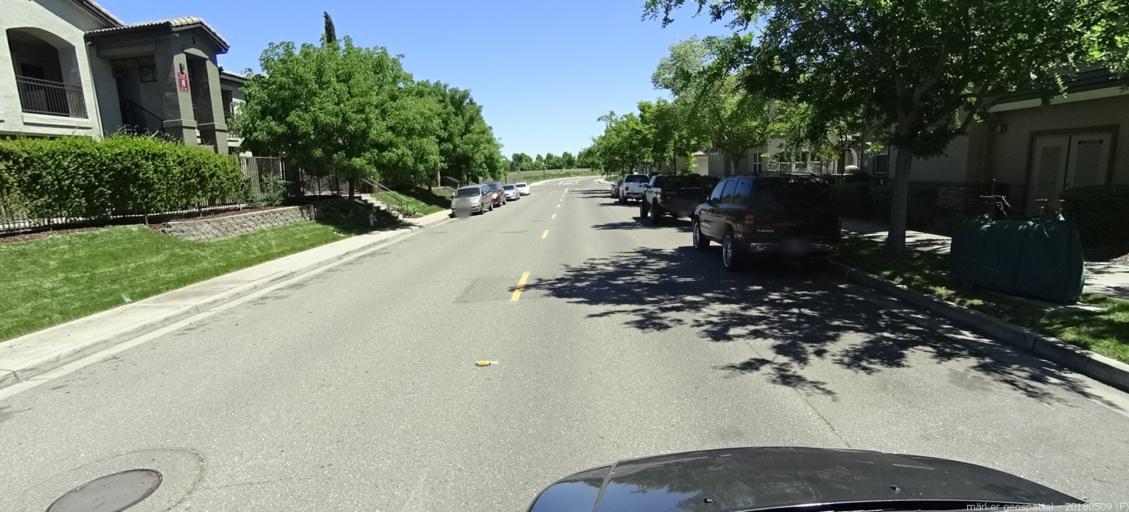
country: US
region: California
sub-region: Sacramento County
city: Sacramento
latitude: 38.6433
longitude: -121.5124
